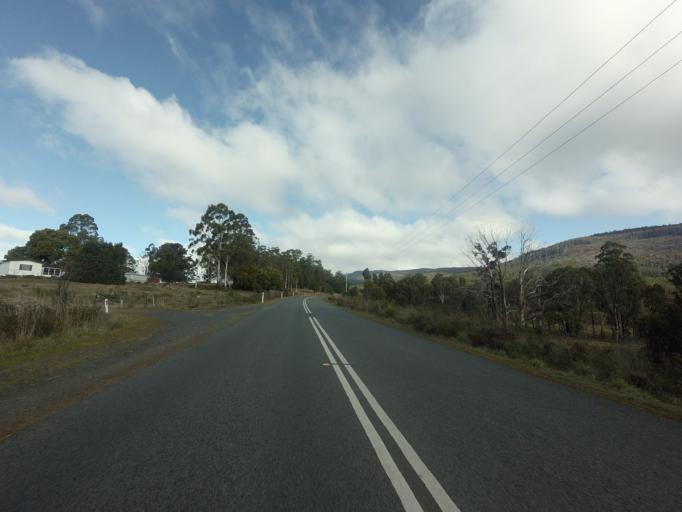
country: AU
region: Tasmania
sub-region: Derwent Valley
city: New Norfolk
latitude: -42.5835
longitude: 146.6940
